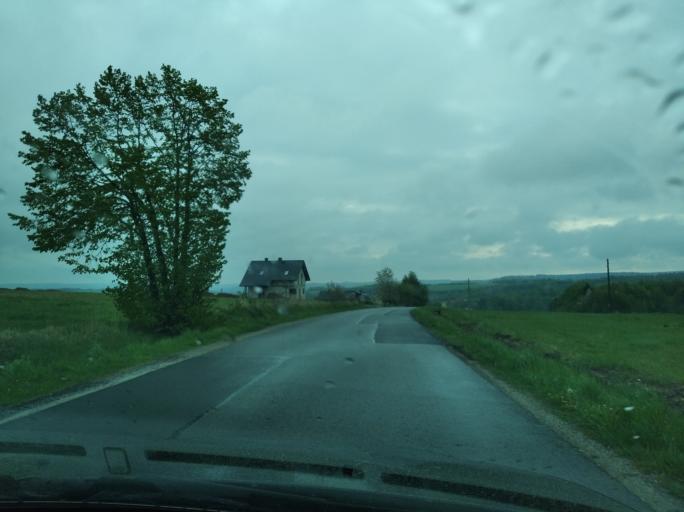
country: PL
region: Subcarpathian Voivodeship
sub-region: Powiat rzeszowski
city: Straszydle
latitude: 49.8772
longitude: 21.9851
